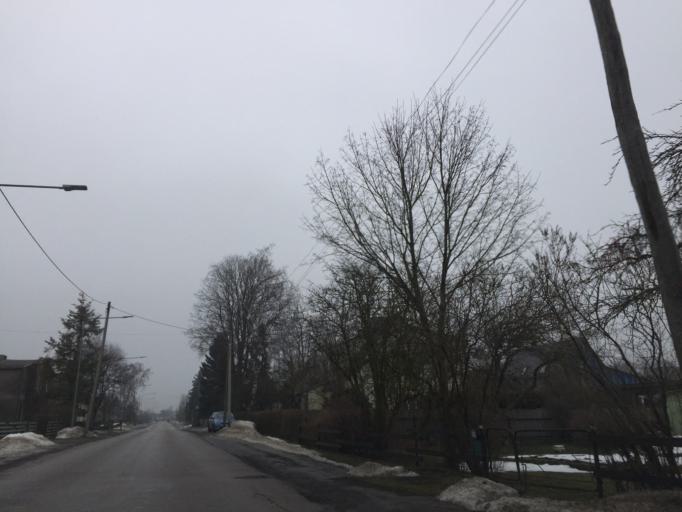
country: EE
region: Saare
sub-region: Kuressaare linn
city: Kuressaare
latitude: 58.2485
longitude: 22.4944
